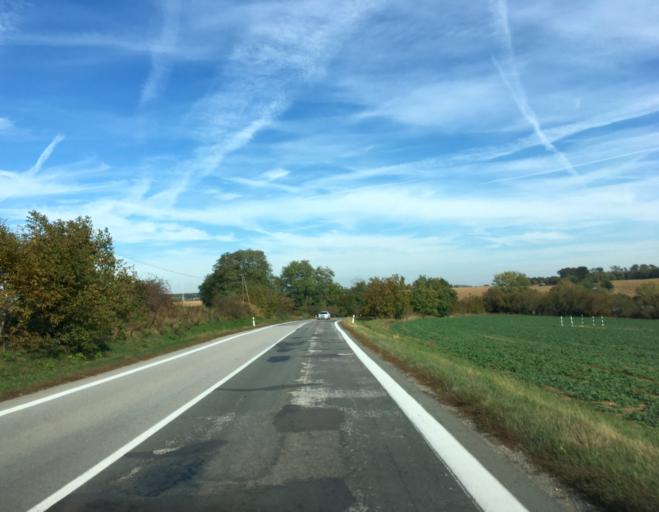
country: SK
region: Nitriansky
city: Svodin
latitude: 48.0284
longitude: 18.4209
